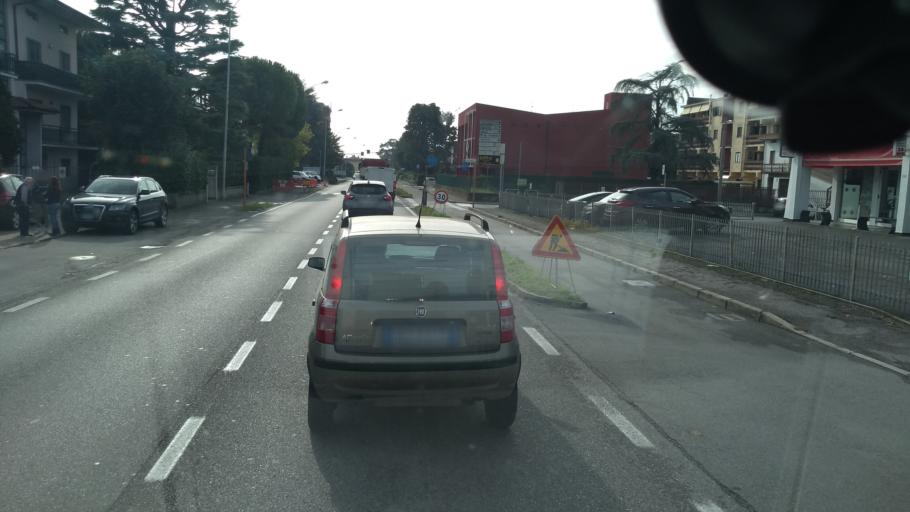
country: IT
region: Lombardy
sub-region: Provincia di Bergamo
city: Urgnano
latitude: 45.6010
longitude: 9.6988
